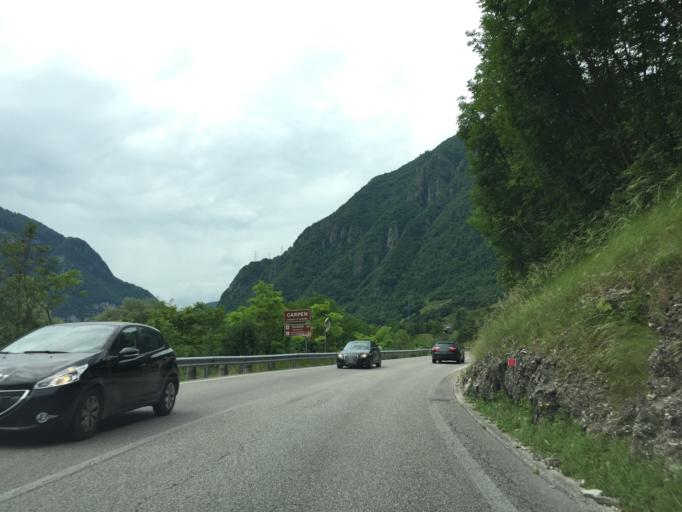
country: IT
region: Veneto
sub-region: Provincia di Belluno
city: Vas
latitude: 45.9732
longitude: 11.9367
